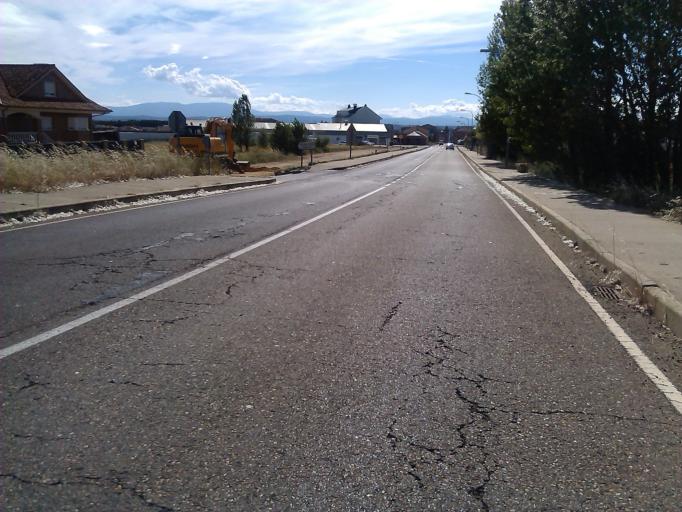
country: ES
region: Castille and Leon
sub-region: Provincia de Leon
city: San Justo de la Vega
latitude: 42.4544
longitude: -6.0080
